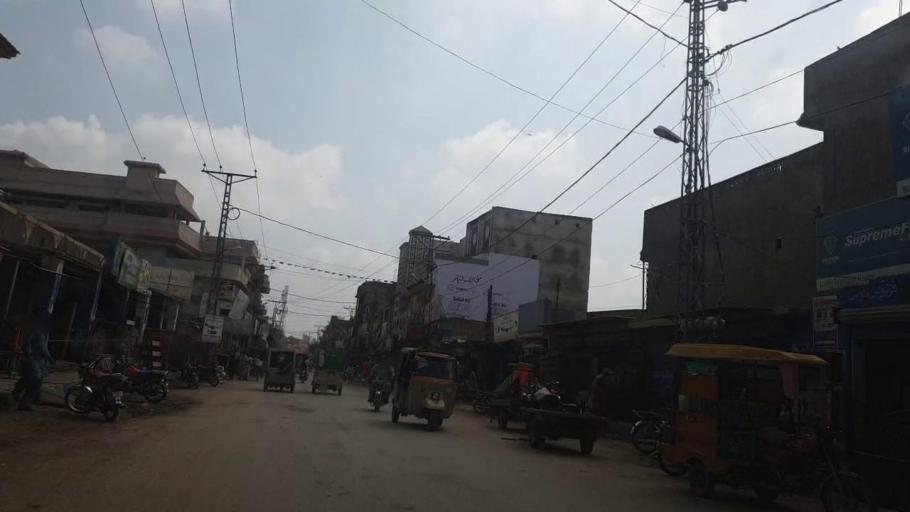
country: PK
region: Sindh
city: Khairpur
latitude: 27.5239
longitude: 68.7524
